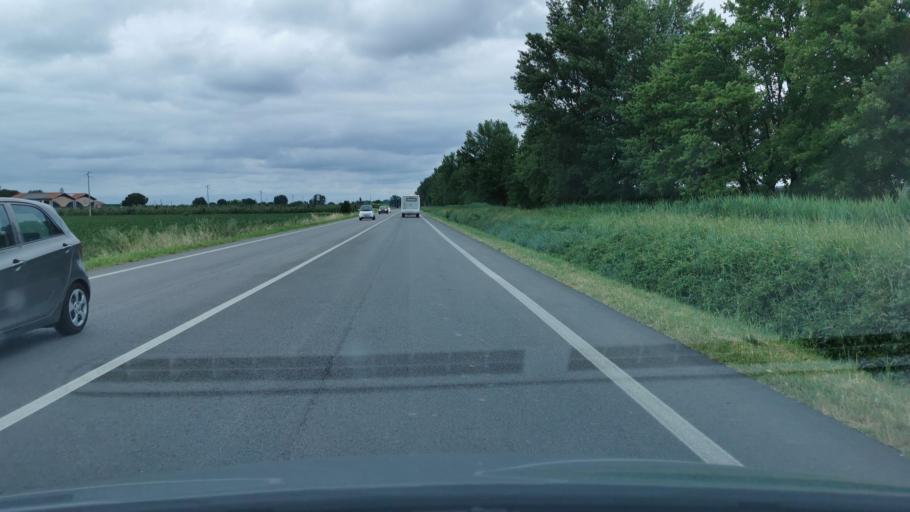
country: IT
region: Emilia-Romagna
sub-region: Provincia di Ravenna
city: Granarolo
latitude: 44.3401
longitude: 11.9194
